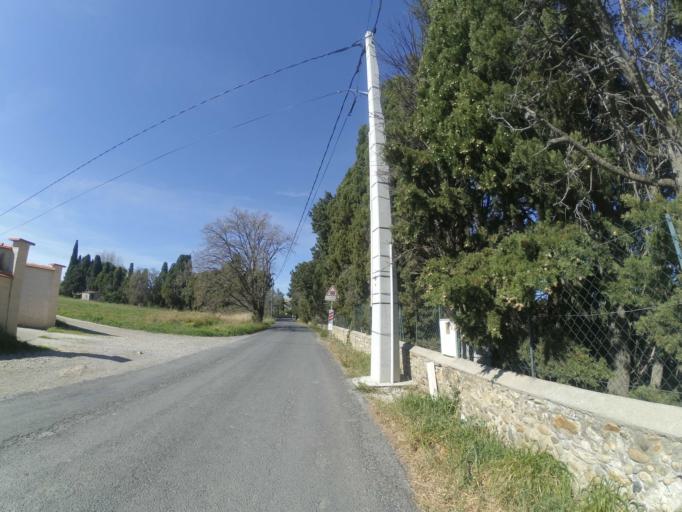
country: FR
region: Languedoc-Roussillon
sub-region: Departement des Pyrenees-Orientales
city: Le Soler
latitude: 42.6778
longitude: 2.7976
